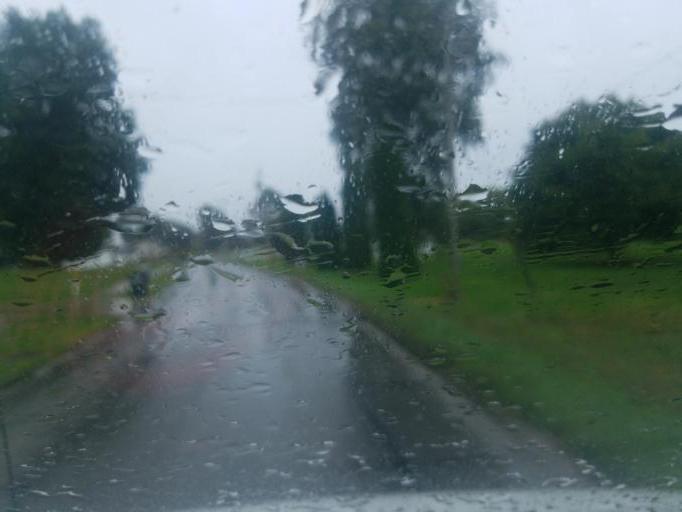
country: US
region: Ohio
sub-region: Wayne County
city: Creston
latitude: 40.9749
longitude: -81.9026
